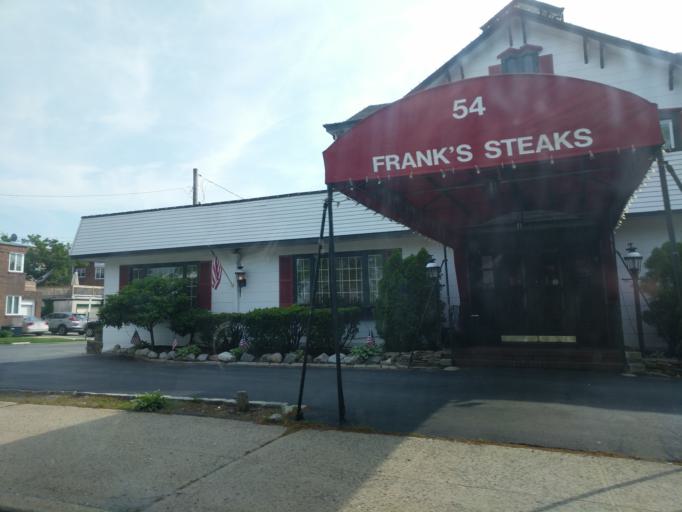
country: US
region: New York
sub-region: Nassau County
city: Rockville Centre
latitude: 40.6553
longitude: -73.6479
